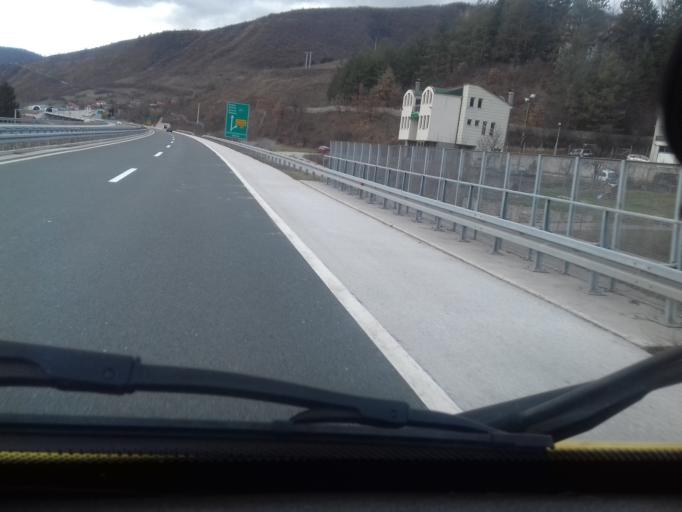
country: BA
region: Federation of Bosnia and Herzegovina
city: Kacuni
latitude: 44.1352
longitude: 17.9990
